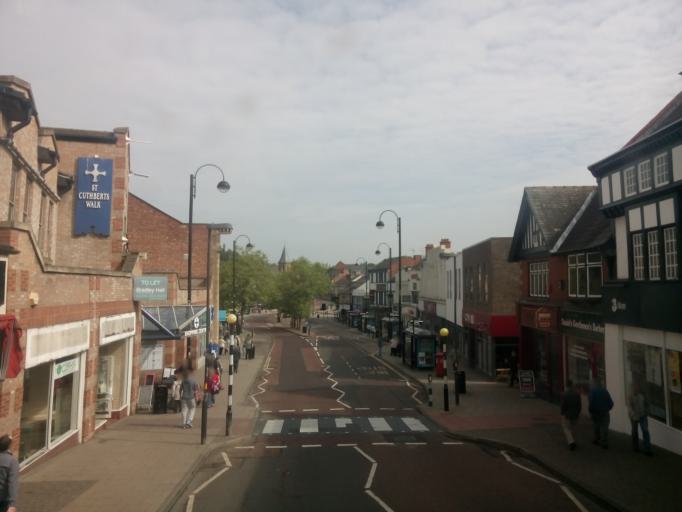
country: GB
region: England
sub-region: County Durham
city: Chester-le-Street
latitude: 54.8571
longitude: -1.5739
